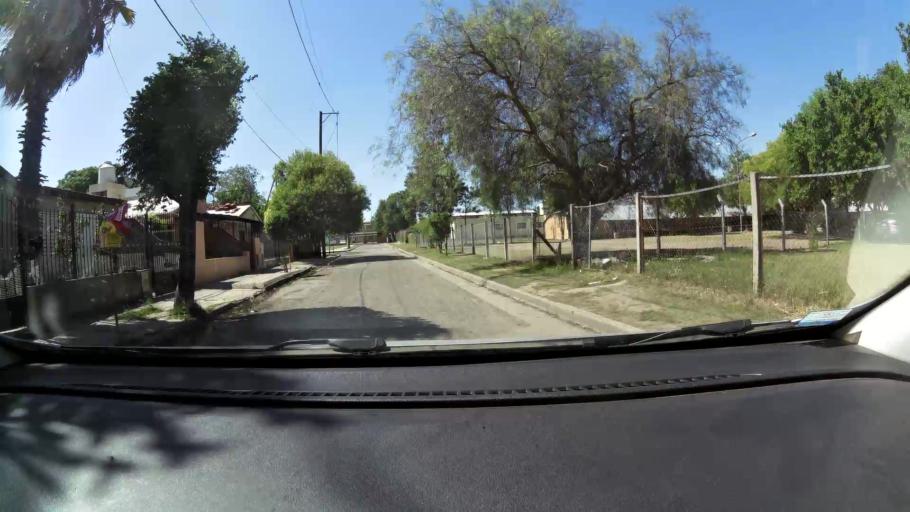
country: AR
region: Cordoba
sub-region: Departamento de Capital
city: Cordoba
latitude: -31.3678
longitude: -64.1356
